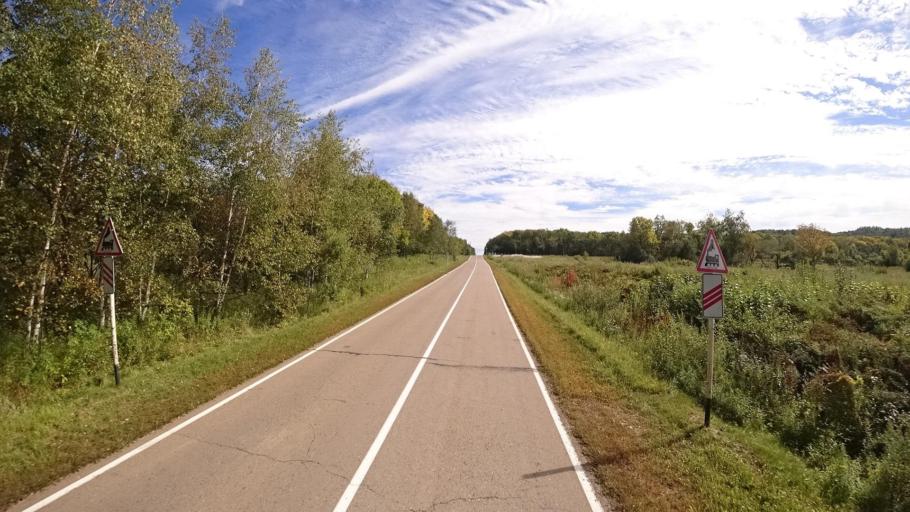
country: RU
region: Primorskiy
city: Yakovlevka
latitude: 44.4077
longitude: 133.5906
